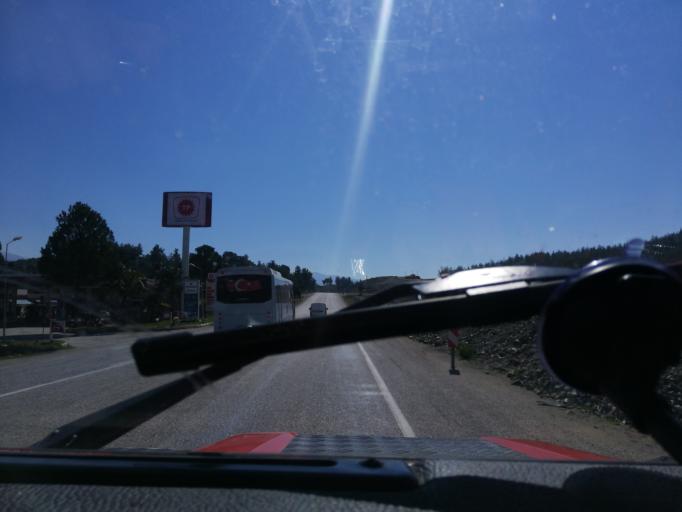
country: TR
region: Mugla
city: Kemer
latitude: 36.6137
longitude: 29.3577
